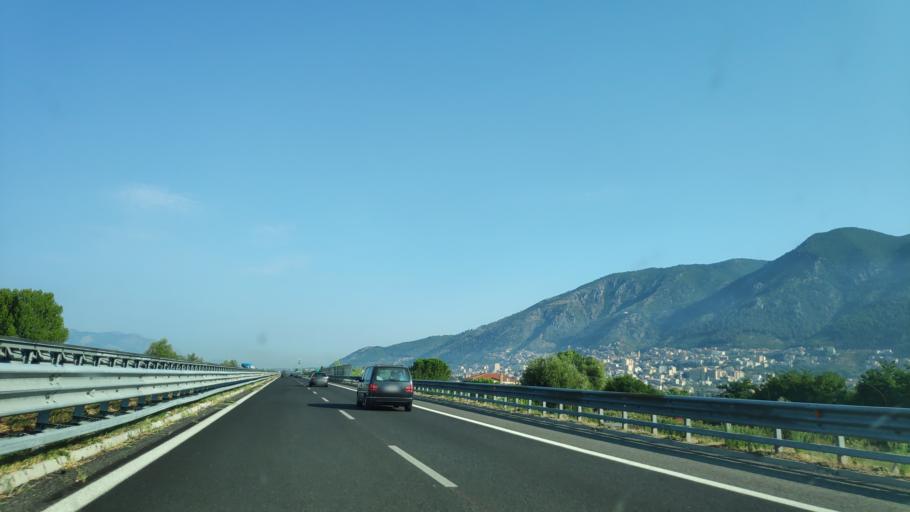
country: IT
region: Campania
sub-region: Provincia di Salerno
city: Sala Consilina
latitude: 40.3773
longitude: 15.5971
